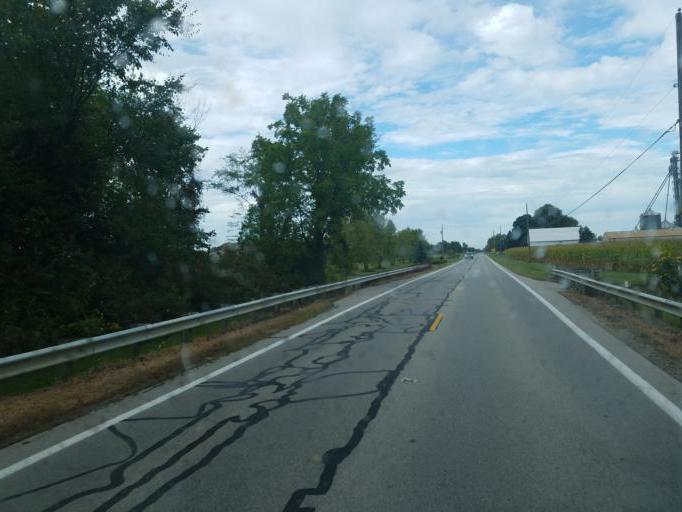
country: US
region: Ohio
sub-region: Delaware County
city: Sunbury
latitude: 40.1826
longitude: -82.8062
